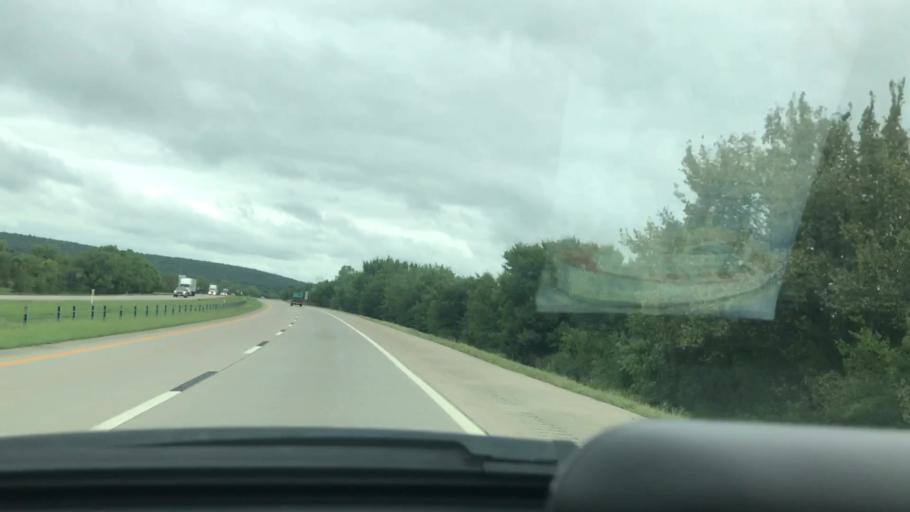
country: US
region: Oklahoma
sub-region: Pittsburg County
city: Krebs
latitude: 35.0069
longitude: -95.7188
